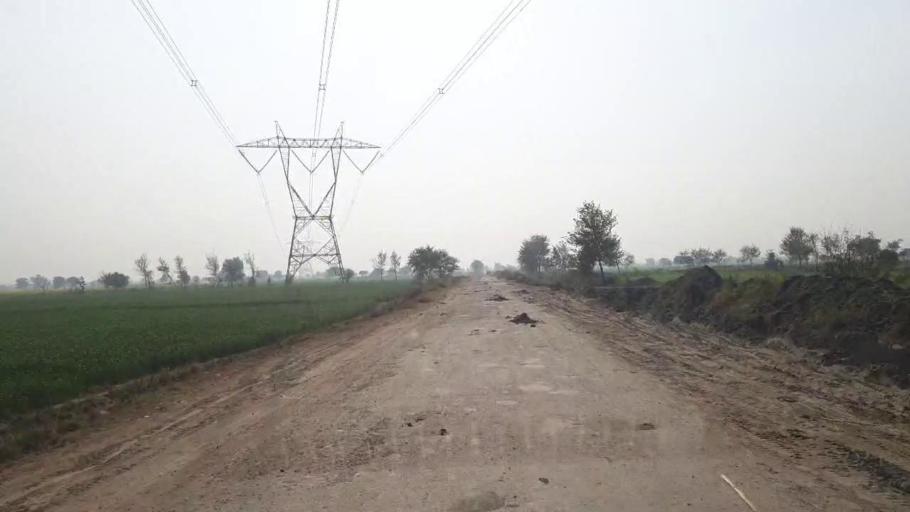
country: PK
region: Sindh
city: Hala
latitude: 25.9382
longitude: 68.4479
